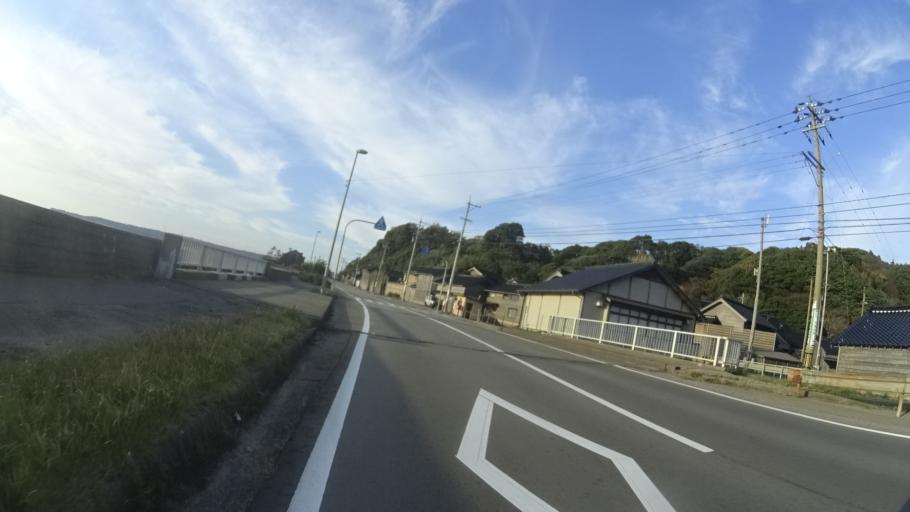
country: JP
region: Ishikawa
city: Hakui
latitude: 37.1267
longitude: 136.7291
